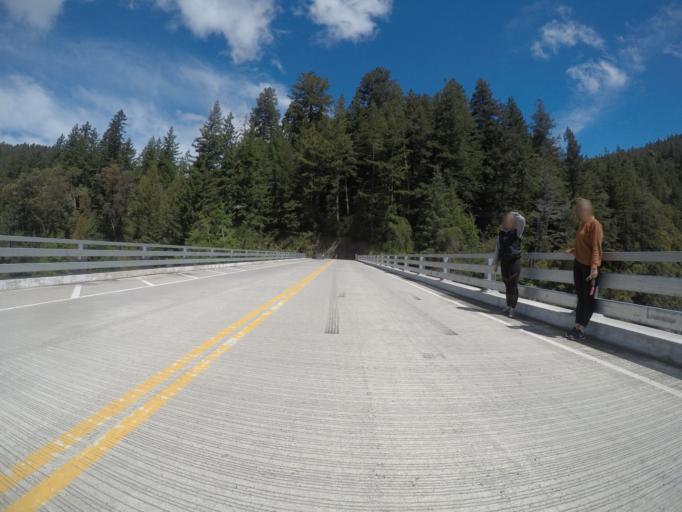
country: US
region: California
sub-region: Del Norte County
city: Bertsch-Oceanview
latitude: 41.7971
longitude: -124.0543
